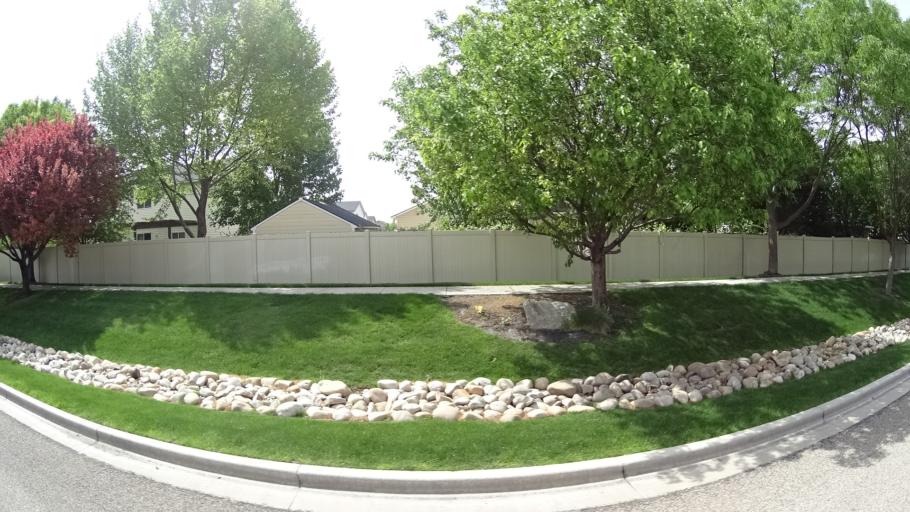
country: US
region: Idaho
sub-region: Ada County
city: Meridian
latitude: 43.5538
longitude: -116.3186
